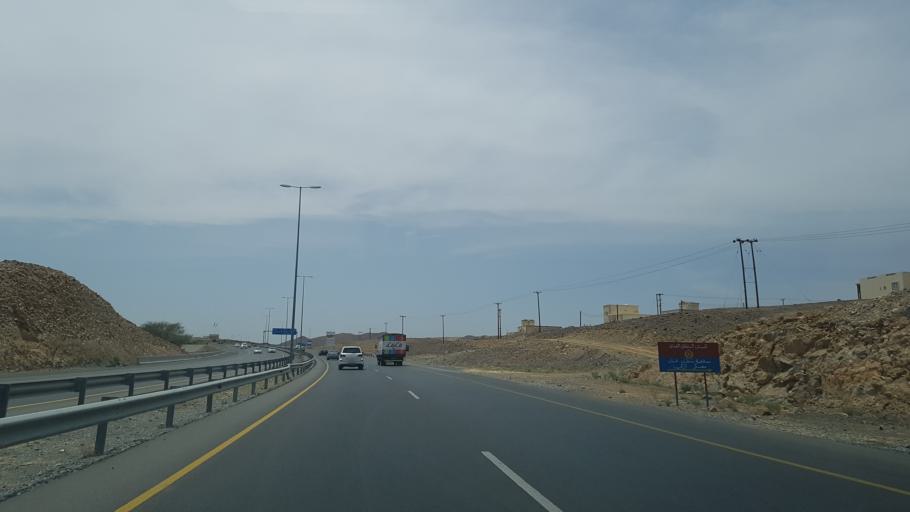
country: OM
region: Muhafazat ad Dakhiliyah
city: Izki
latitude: 22.9105
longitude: 57.7512
